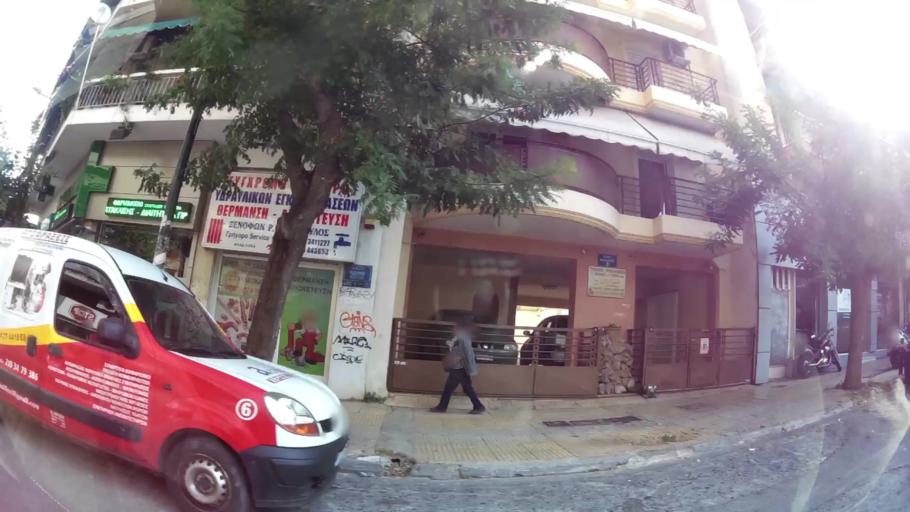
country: GR
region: Attica
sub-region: Nomarchia Athinas
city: Athens
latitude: 37.9668
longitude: 23.7095
